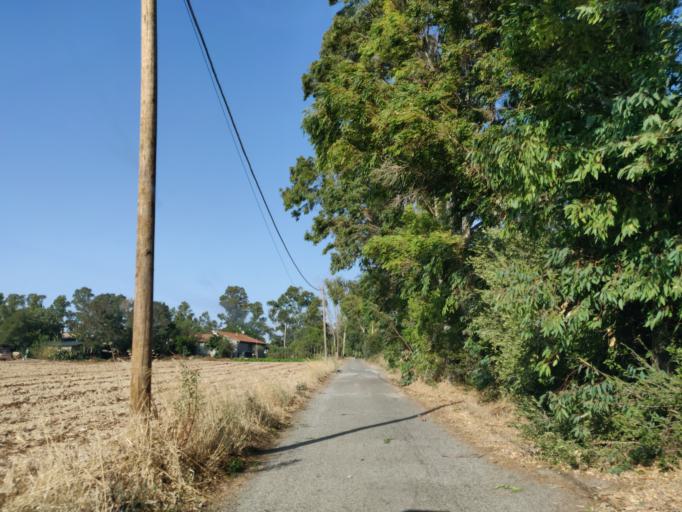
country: IT
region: Latium
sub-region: Citta metropolitana di Roma Capitale
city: Aurelia
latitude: 42.1397
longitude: 11.7645
